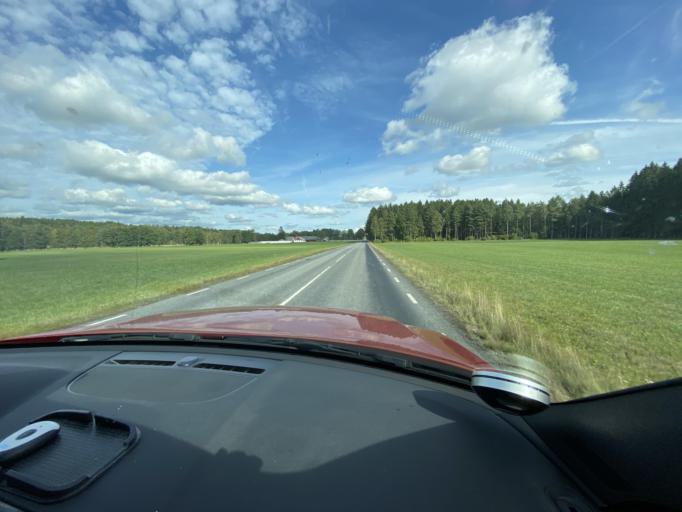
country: SE
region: Skane
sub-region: Hassleholms Kommun
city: Bjarnum
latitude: 56.3556
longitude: 13.7786
